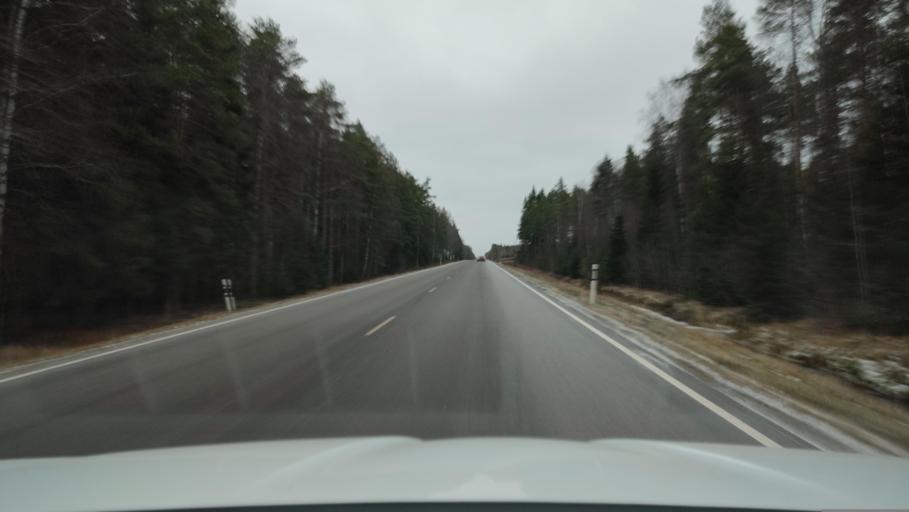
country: FI
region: Ostrobothnia
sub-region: Sydosterbotten
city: Naerpes
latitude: 62.5701
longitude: 21.4863
